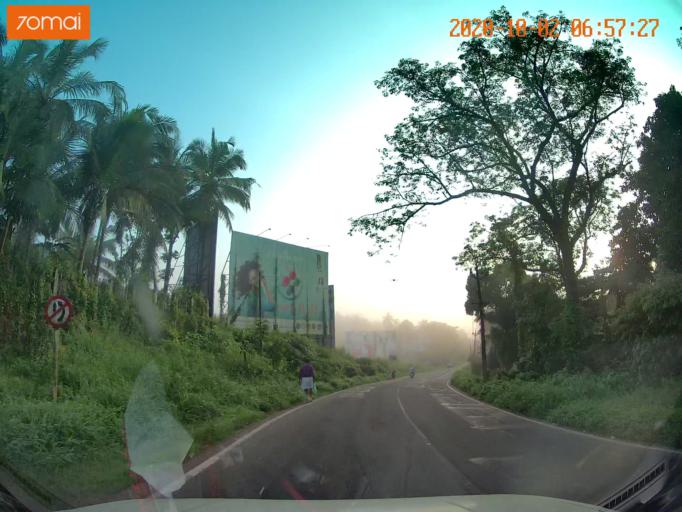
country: IN
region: Kerala
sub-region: Malappuram
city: Tirur
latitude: 10.8695
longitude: 76.0533
